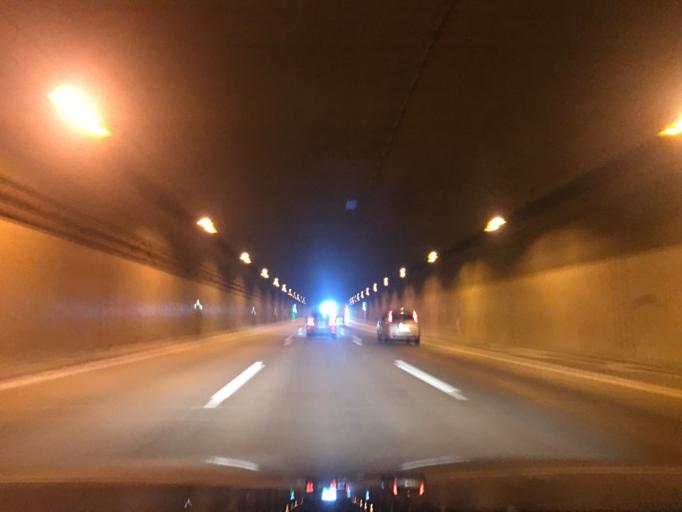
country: DE
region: North Rhine-Westphalia
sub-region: Regierungsbezirk Dusseldorf
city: Meerbusch
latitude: 51.2868
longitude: 6.6786
